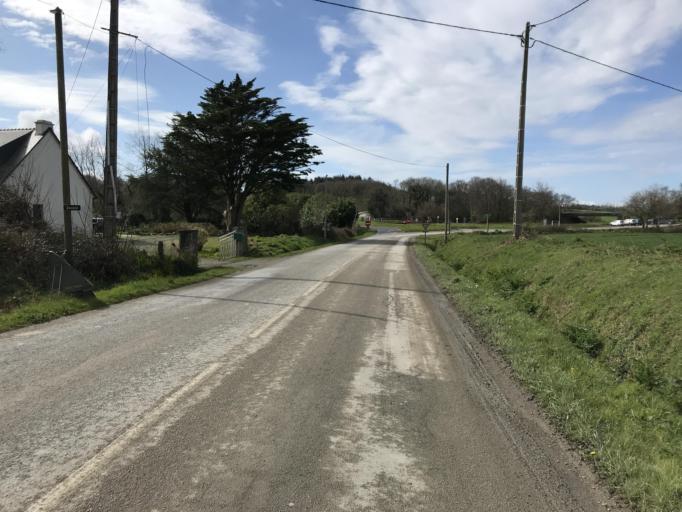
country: FR
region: Brittany
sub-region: Departement du Finistere
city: Daoulas
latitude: 48.3769
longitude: -4.2712
